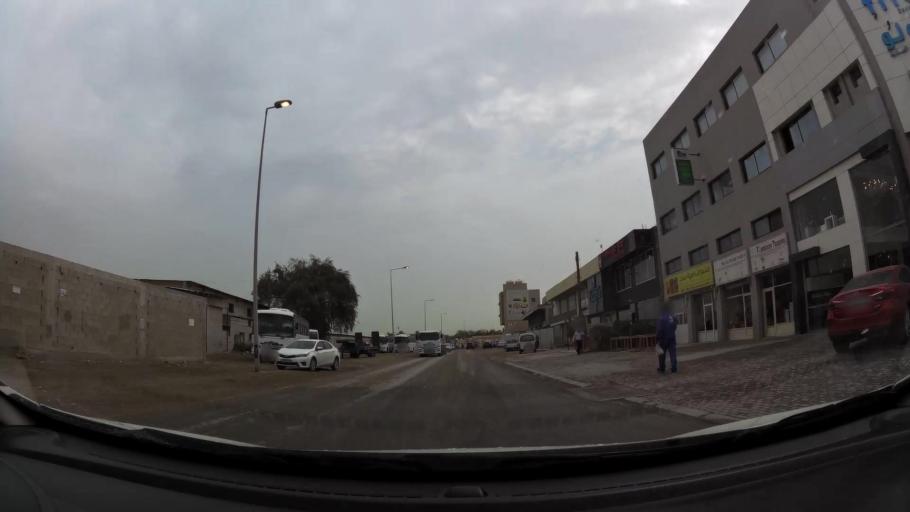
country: BH
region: Northern
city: Ar Rifa'
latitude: 26.1385
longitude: 50.5884
